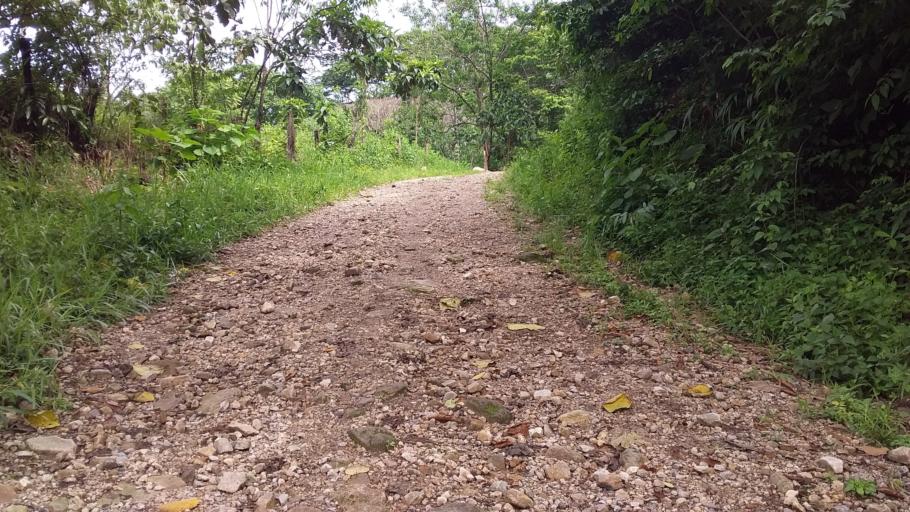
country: CO
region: Casanare
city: Nunchia
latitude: 5.6441
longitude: -72.2954
